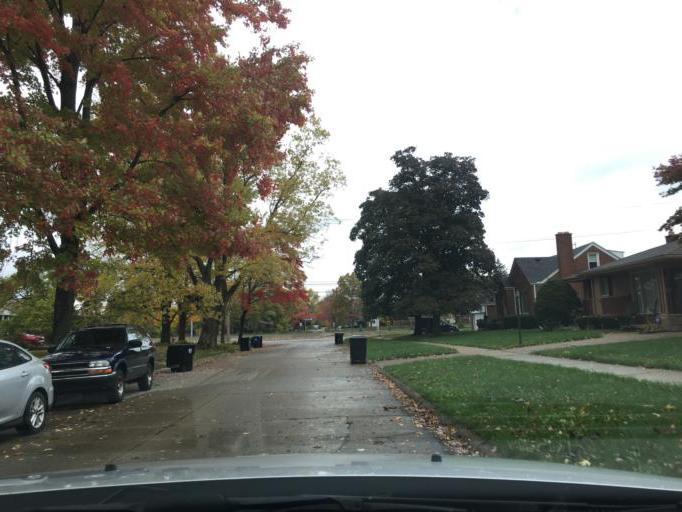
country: US
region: Michigan
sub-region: Wayne County
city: Redford
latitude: 42.3838
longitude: -83.2929
